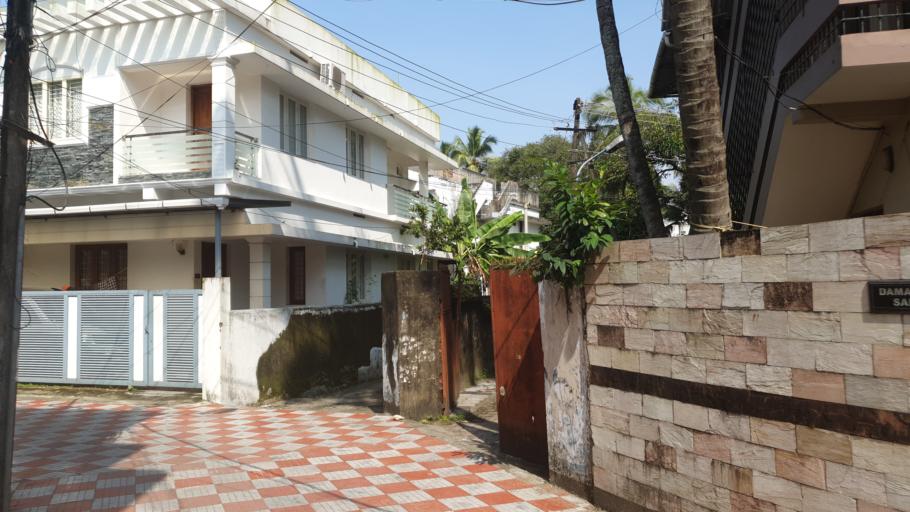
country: IN
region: Kerala
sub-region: Ernakulam
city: Cochin
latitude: 9.9591
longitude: 76.2562
